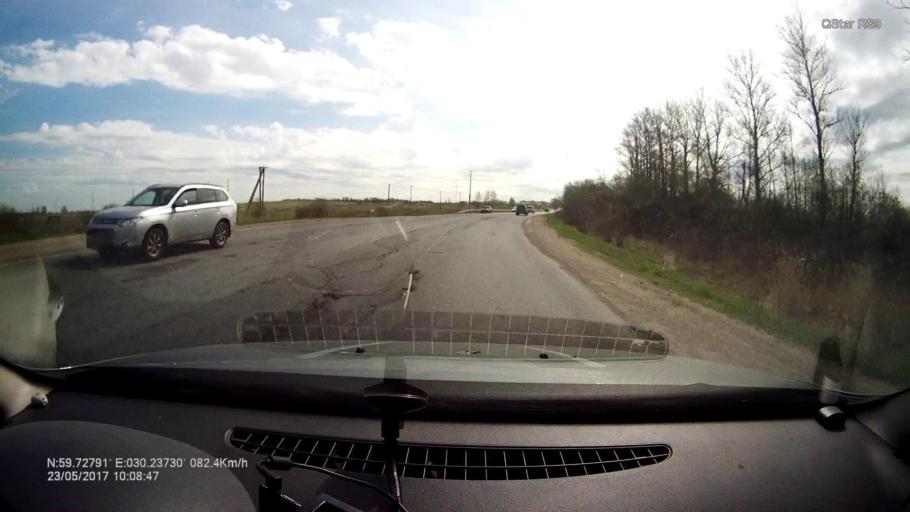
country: RU
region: St.-Petersburg
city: Aleksandrovskaya
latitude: 59.7279
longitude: 30.2374
